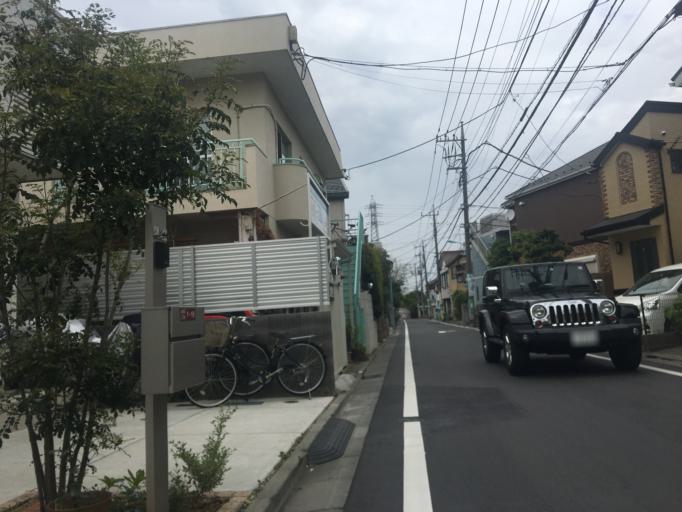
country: JP
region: Tokyo
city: Tokyo
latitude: 35.6864
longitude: 139.6300
